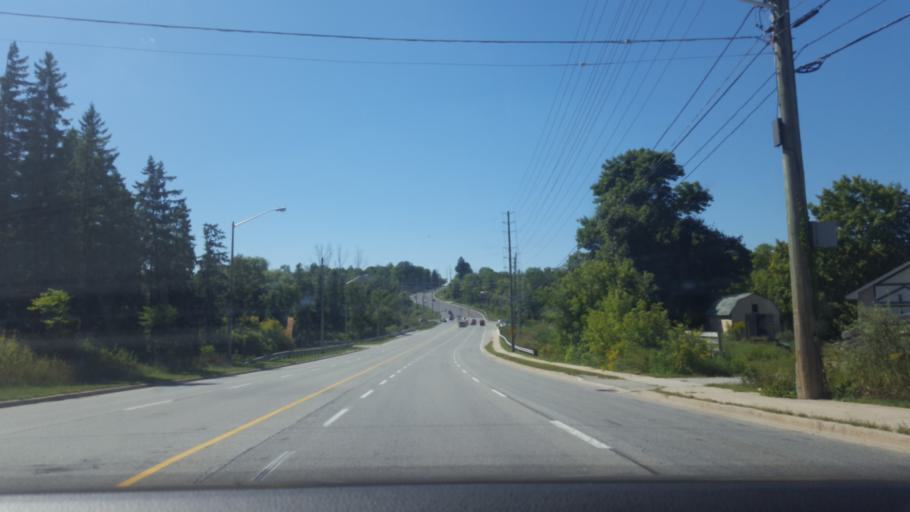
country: CA
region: Ontario
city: Vaughan
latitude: 43.8123
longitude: -79.6253
